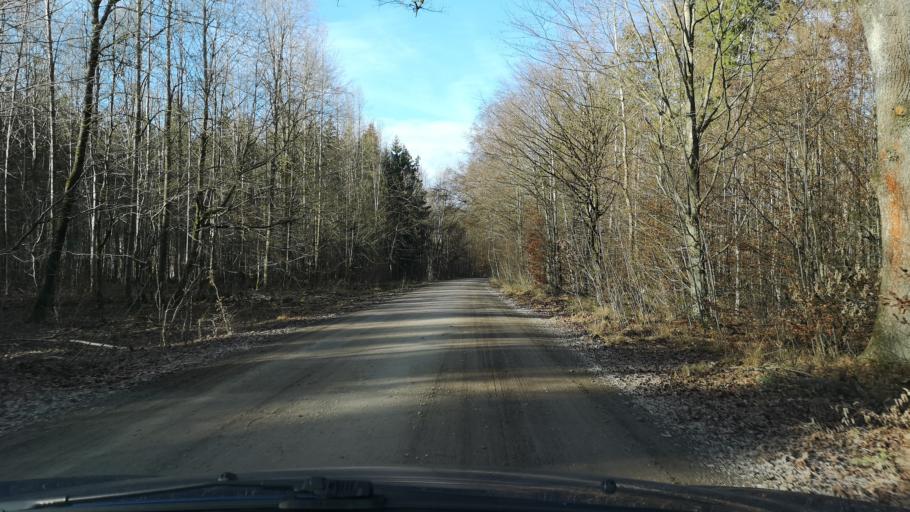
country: DE
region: Bavaria
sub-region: Upper Bavaria
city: Ebersberg
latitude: 48.1040
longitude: 11.9354
